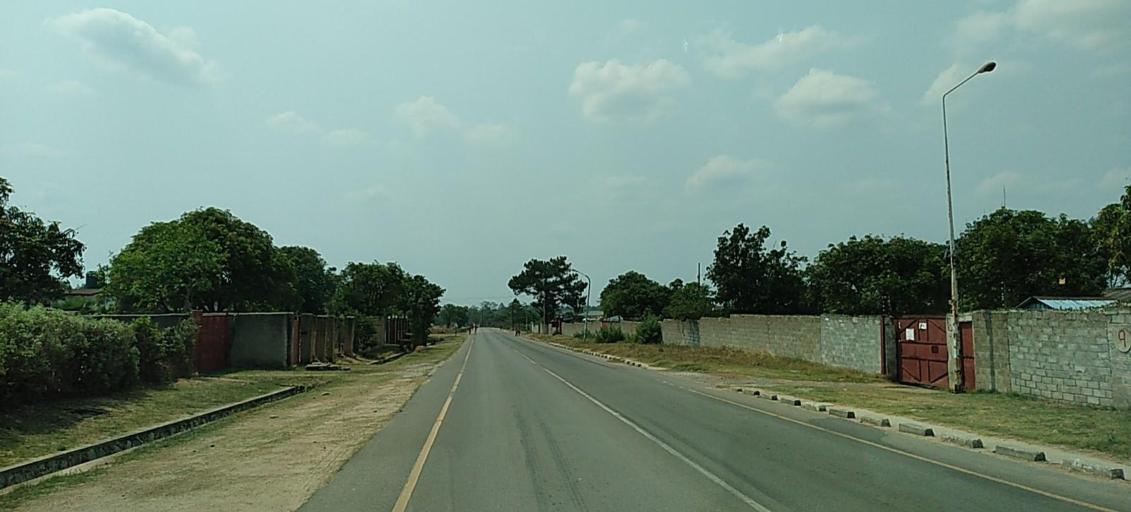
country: ZM
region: Copperbelt
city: Chambishi
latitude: -12.6369
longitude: 28.0581
